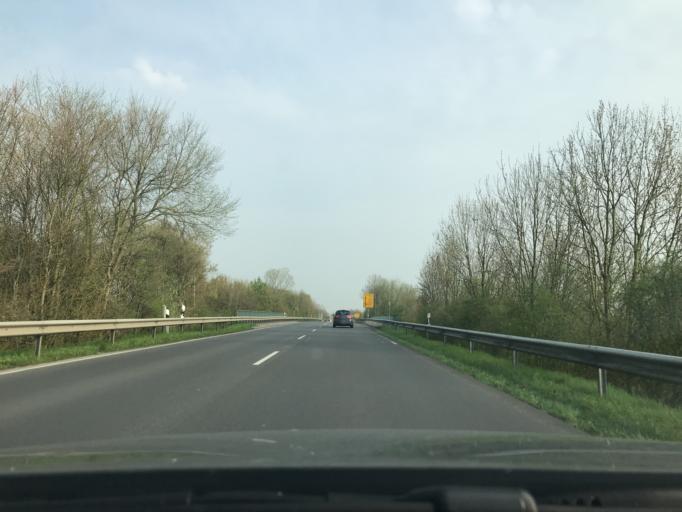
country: DE
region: North Rhine-Westphalia
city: Geldern
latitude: 51.5056
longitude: 6.3040
